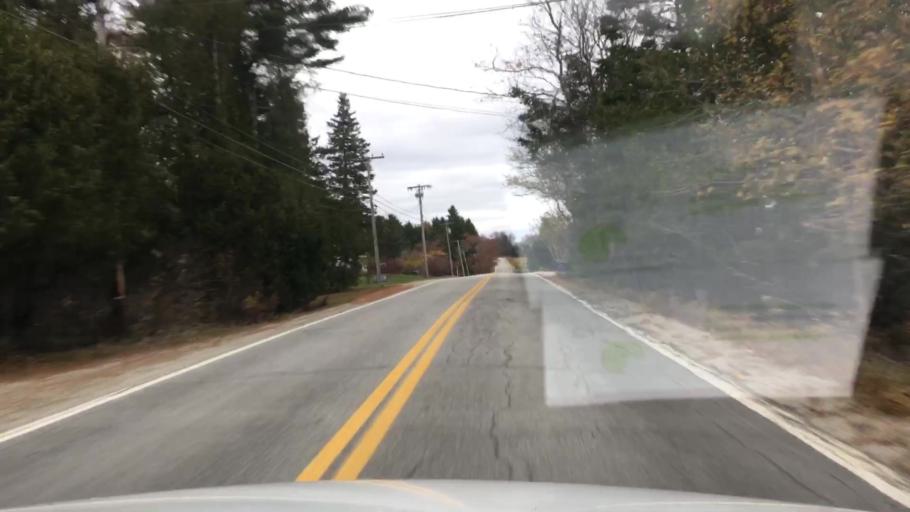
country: US
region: Maine
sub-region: Hancock County
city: Sedgwick
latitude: 44.3466
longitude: -68.5554
